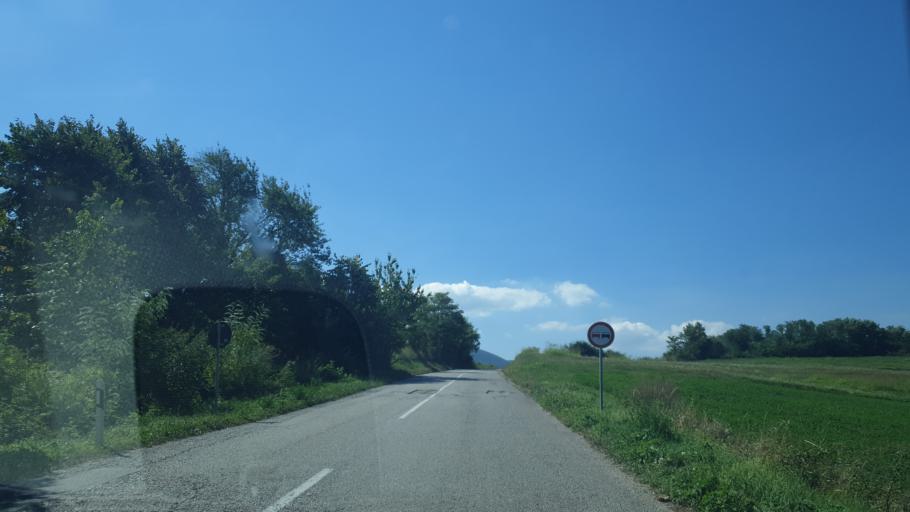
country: RS
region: Central Serbia
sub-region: Kolubarski Okrug
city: Mionica
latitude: 44.1791
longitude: 20.0483
